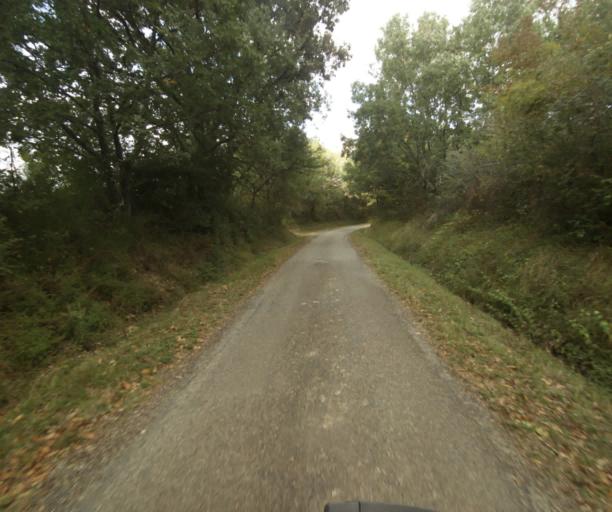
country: FR
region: Midi-Pyrenees
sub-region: Departement de la Haute-Garonne
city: Launac
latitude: 43.8308
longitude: 1.1157
